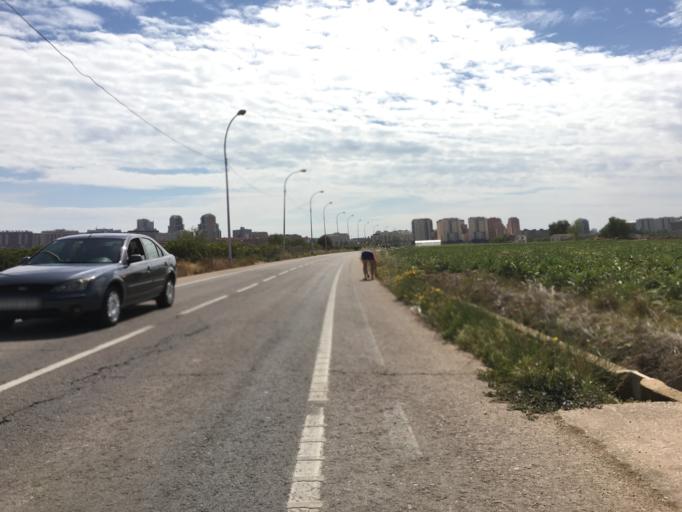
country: ES
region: Valencia
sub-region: Provincia de Valencia
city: Mislata
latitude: 39.4904
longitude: -0.4161
